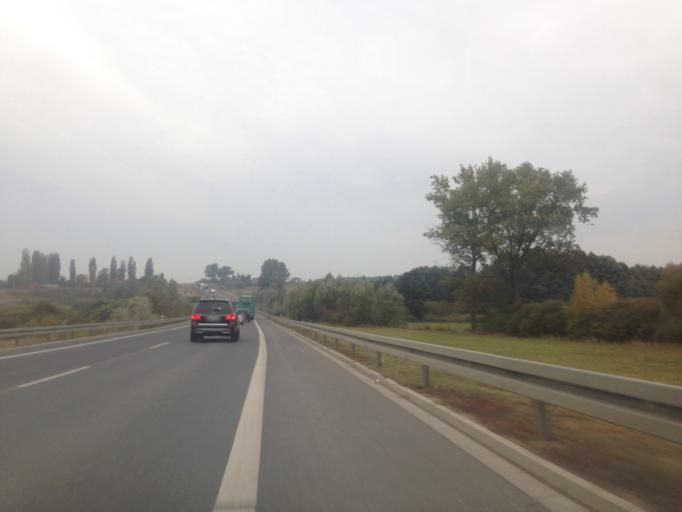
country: PL
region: Greater Poland Voivodeship
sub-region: Powiat gnieznienski
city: Niechanowo
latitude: 52.5549
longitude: 17.6943
